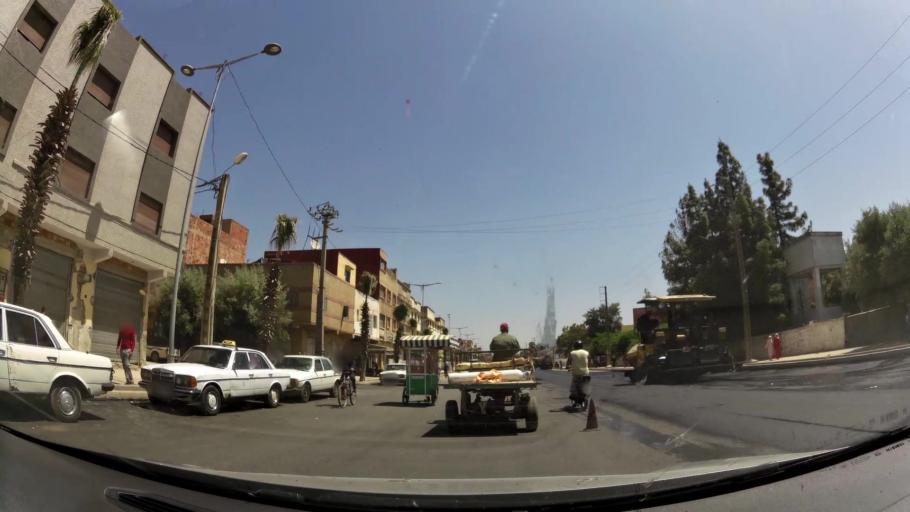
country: MA
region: Rabat-Sale-Zemmour-Zaer
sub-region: Khemisset
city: Khemisset
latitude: 33.8308
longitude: -6.0688
